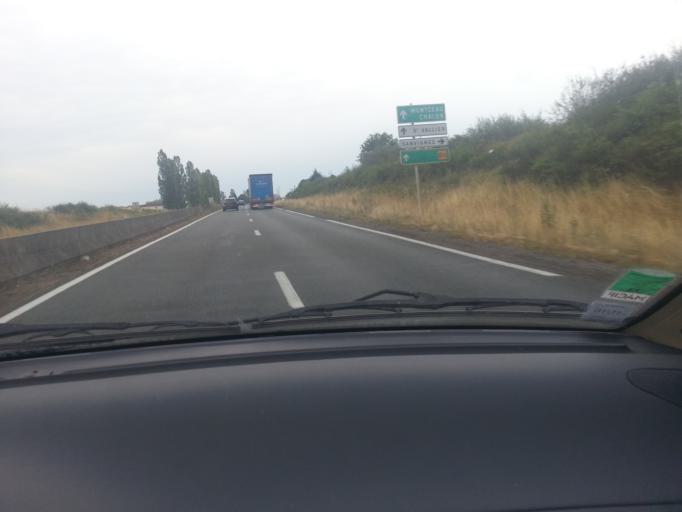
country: FR
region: Bourgogne
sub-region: Departement de Saone-et-Loire
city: Ciry-le-Noble
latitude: 46.6223
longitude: 4.2921
